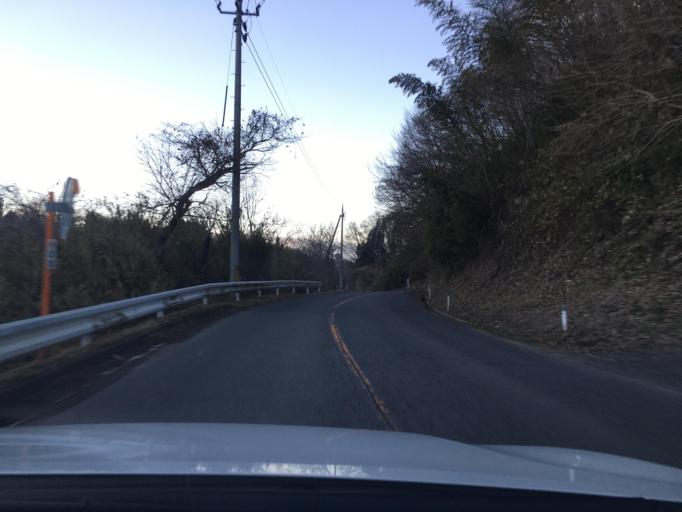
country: JP
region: Fukushima
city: Miharu
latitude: 37.4508
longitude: 140.5081
